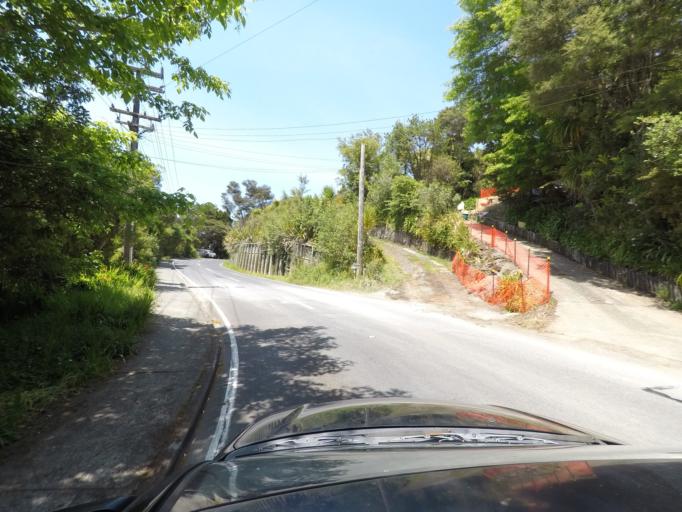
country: NZ
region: Auckland
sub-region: Auckland
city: Titirangi
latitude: -36.9601
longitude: 174.6418
